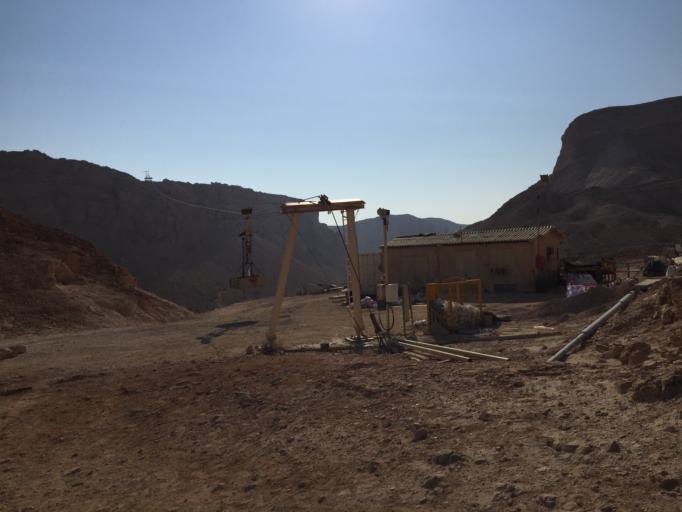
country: IL
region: Southern District
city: `En Boqeq
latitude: 31.3176
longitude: 35.3490
